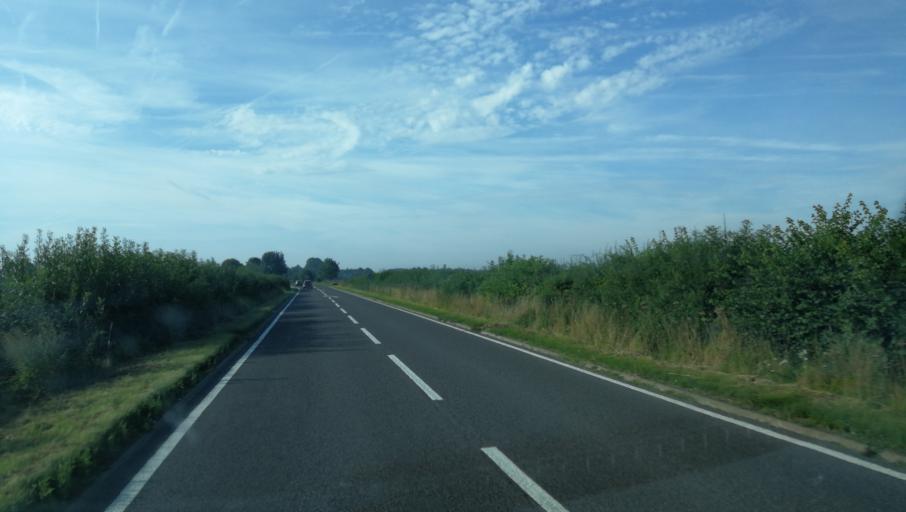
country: GB
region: England
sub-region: Oxfordshire
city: Deddington
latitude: 51.9322
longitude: -1.3257
